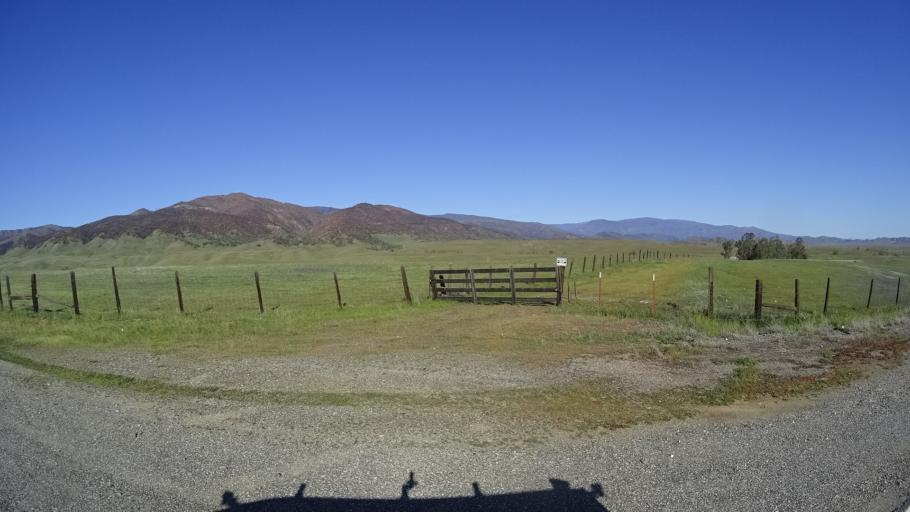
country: US
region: California
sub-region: Tehama County
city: Rancho Tehama Reserve
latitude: 39.7429
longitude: -122.5427
